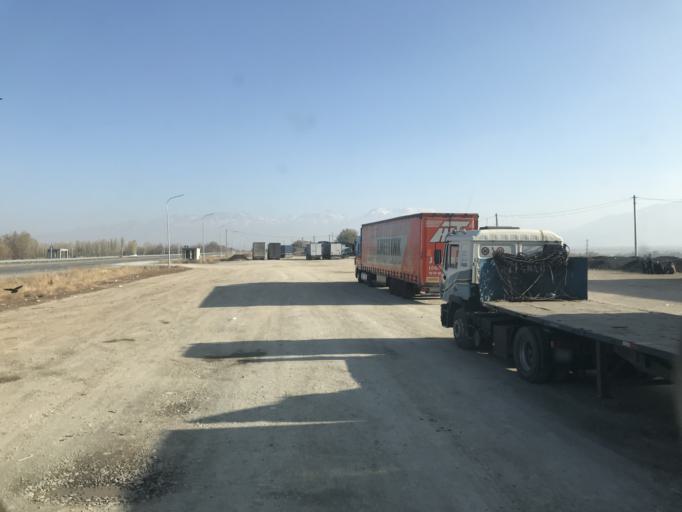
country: KZ
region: Ongtustik Qazaqstan
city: Turar Ryskulov
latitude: 42.5267
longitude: 70.3067
